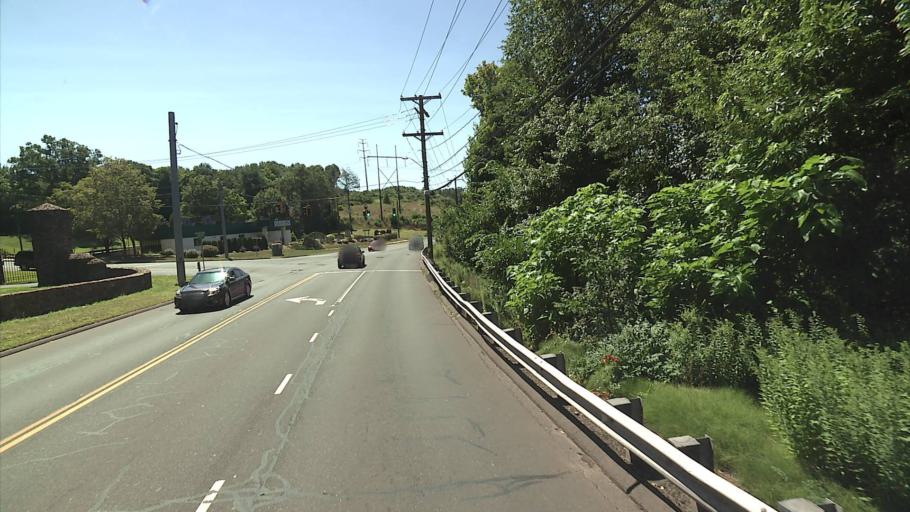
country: US
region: Connecticut
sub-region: Hartford County
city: Plainville
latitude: 41.6168
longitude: -72.8736
